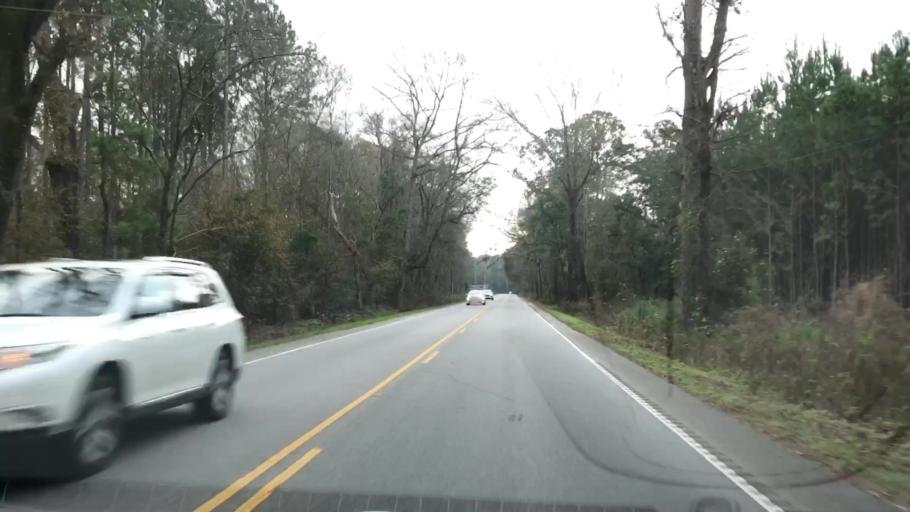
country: US
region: South Carolina
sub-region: Jasper County
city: Ridgeland
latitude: 32.5665
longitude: -80.9170
